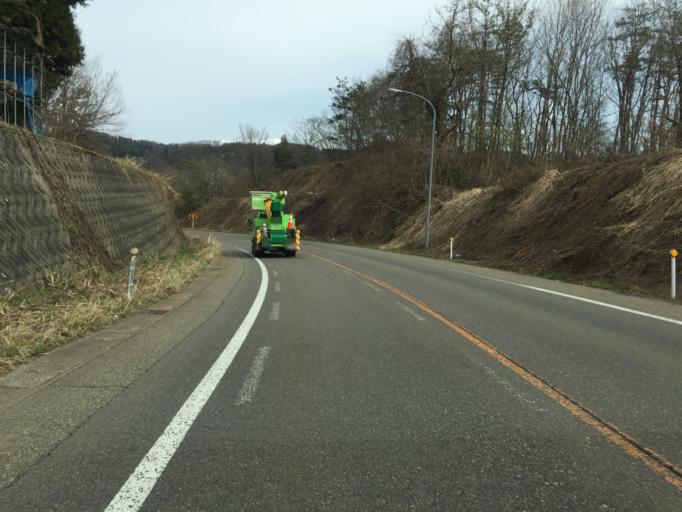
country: JP
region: Niigata
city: Tochio-honcho
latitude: 37.4601
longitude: 138.9777
